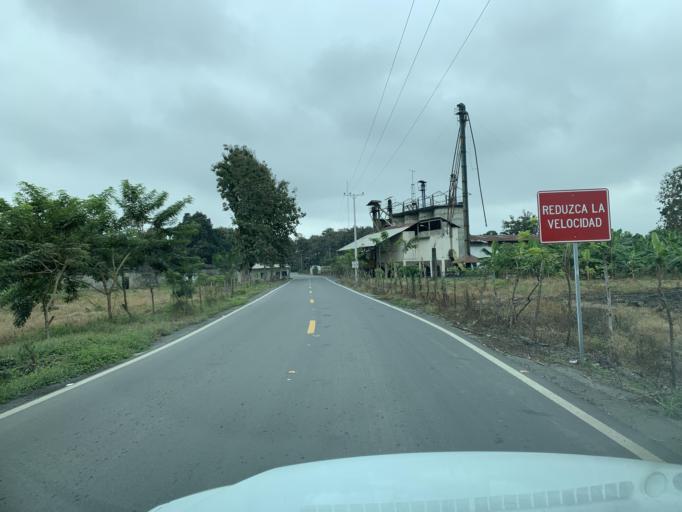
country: EC
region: Guayas
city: Coronel Marcelino Mariduena
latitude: -2.2957
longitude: -79.5037
